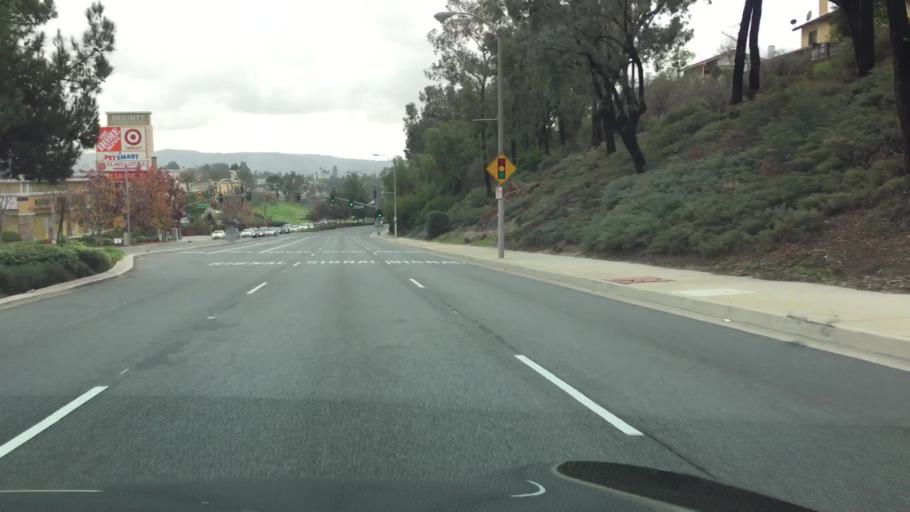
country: US
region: California
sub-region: Los Angeles County
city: South San Jose Hills
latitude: 34.0370
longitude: -117.9131
